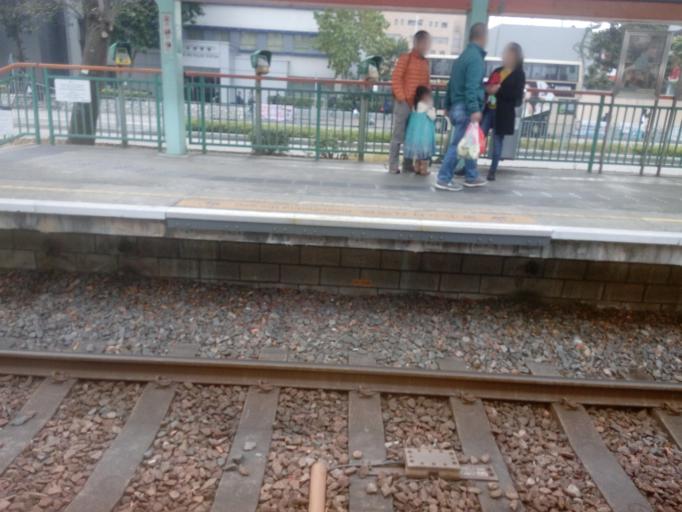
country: HK
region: Yuen Long
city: Yuen Long Kau Hui
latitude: 22.4503
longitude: 114.0030
